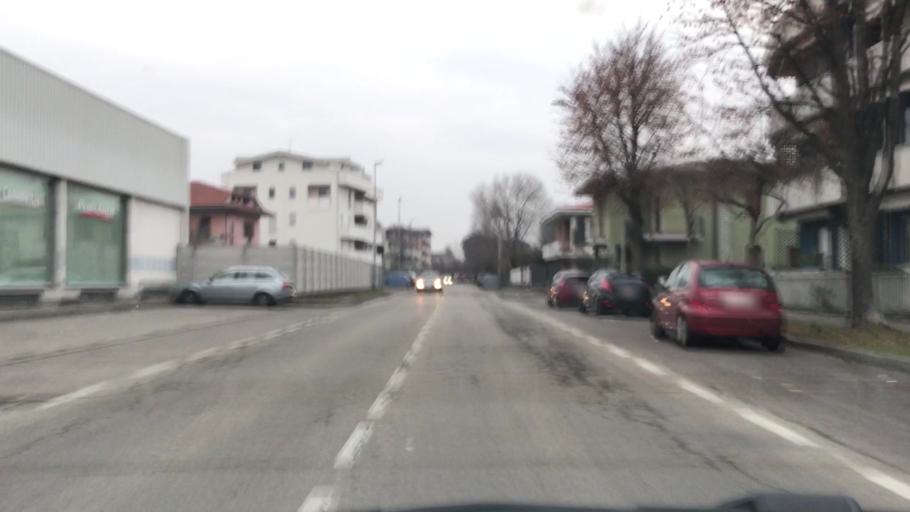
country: IT
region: Lombardy
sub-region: Provincia di Monza e Brianza
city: Seveso
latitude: 45.6427
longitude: 9.1448
